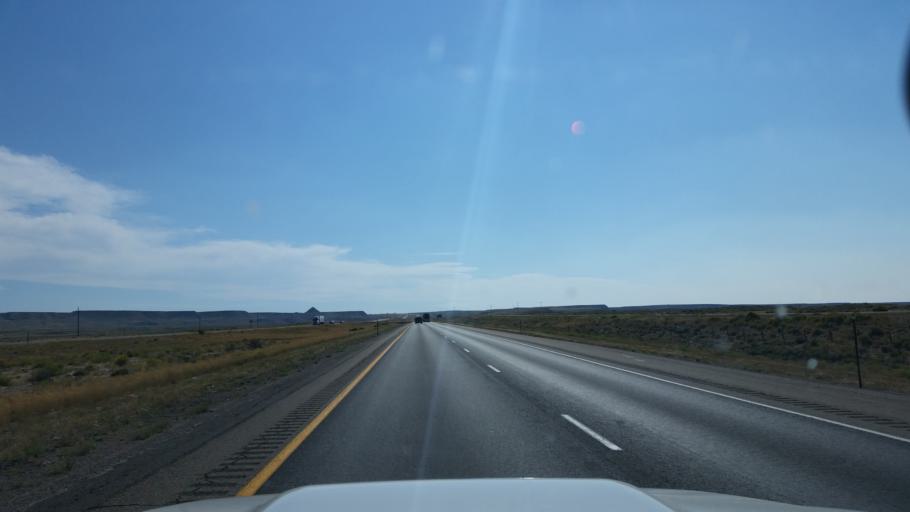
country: US
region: Wyoming
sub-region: Uinta County
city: Lyman
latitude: 41.5168
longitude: -109.9715
